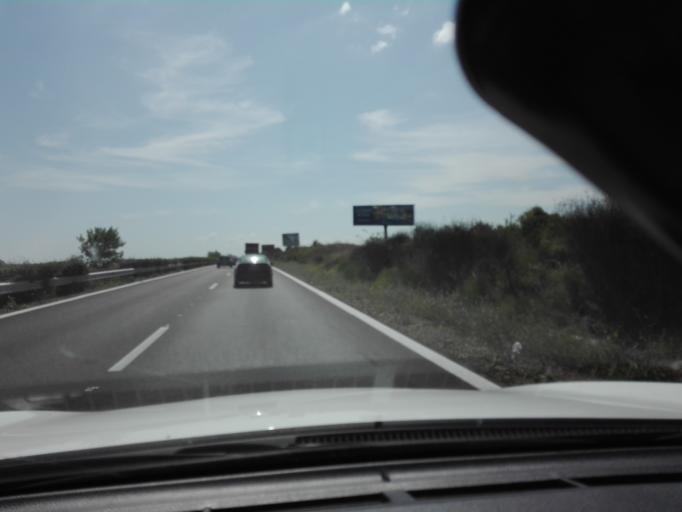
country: BG
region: Burgas
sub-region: Obshtina Burgas
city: Burgas
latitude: 42.5667
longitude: 27.4177
